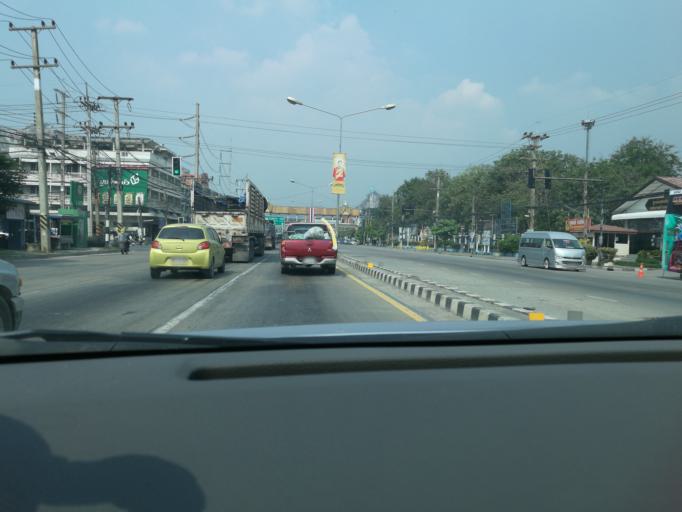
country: TH
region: Sara Buri
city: Chaloem Phra Kiat
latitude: 14.6875
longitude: 100.8712
